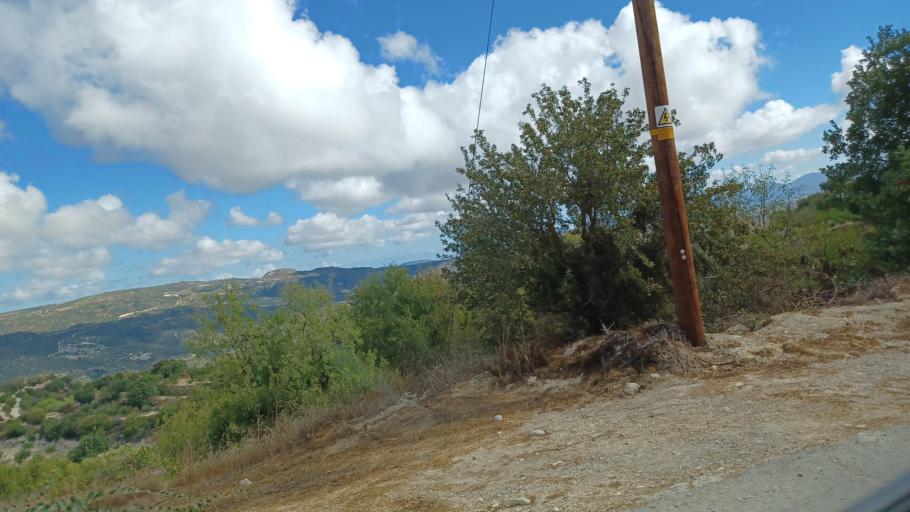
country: CY
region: Pafos
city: Tala
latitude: 34.8578
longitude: 32.4491
